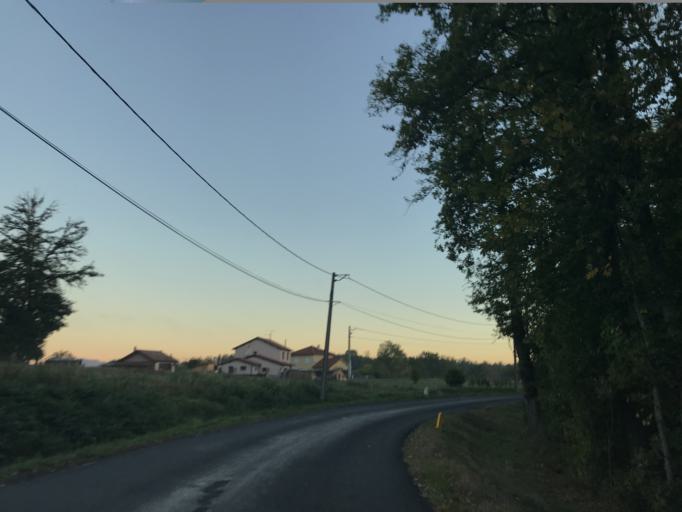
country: FR
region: Auvergne
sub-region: Departement du Puy-de-Dome
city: Celles-sur-Durolle
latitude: 45.8507
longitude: 3.6329
